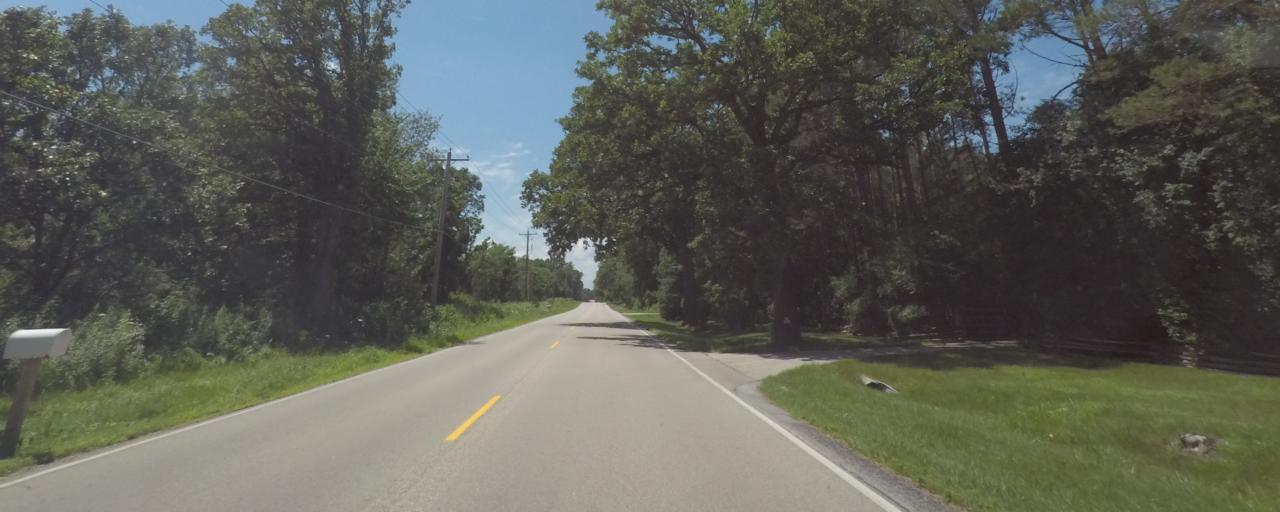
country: US
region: Wisconsin
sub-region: Waukesha County
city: Dousman
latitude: 42.9519
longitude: -88.4820
